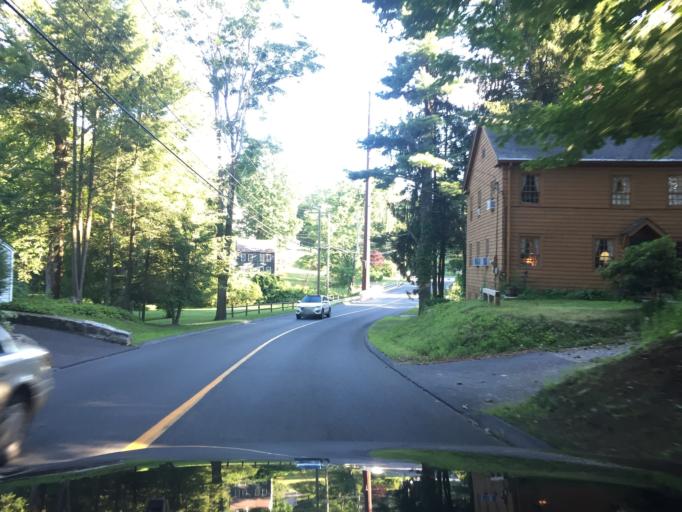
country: US
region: Connecticut
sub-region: Fairfield County
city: Bethel
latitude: 41.3918
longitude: -73.3982
